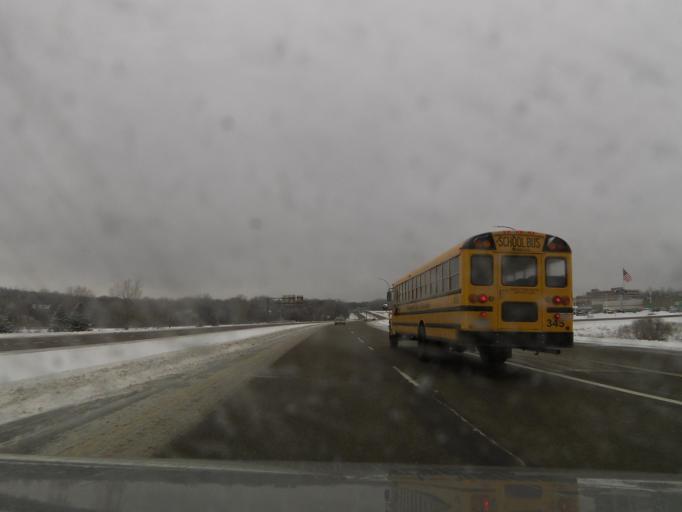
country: US
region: Minnesota
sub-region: Dakota County
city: West Saint Paul
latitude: 44.8777
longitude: -93.0811
